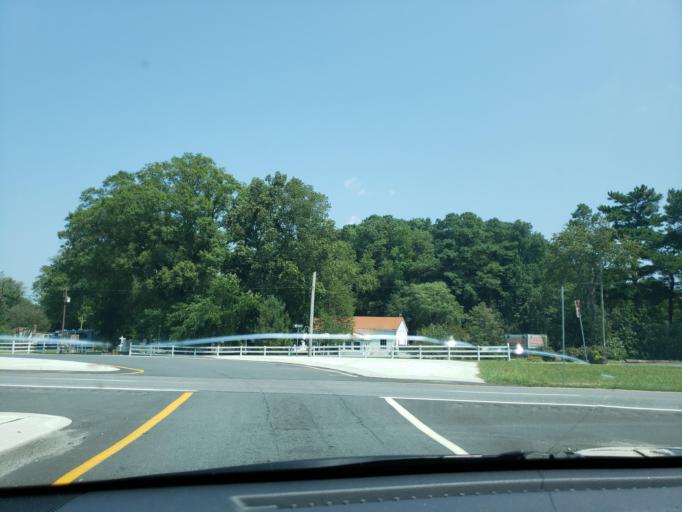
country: US
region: Delaware
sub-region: Sussex County
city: Milton
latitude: 38.8214
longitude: -75.3067
